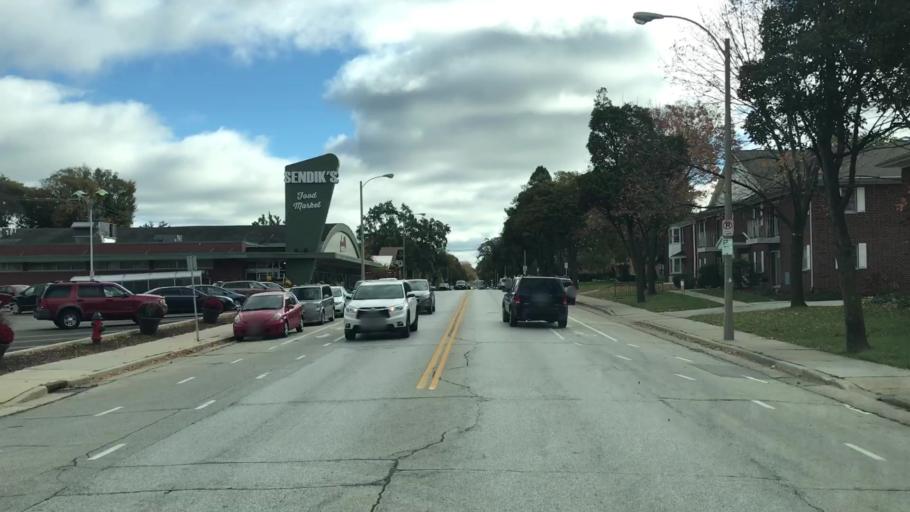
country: US
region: Wisconsin
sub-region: Milwaukee County
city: Wauwatosa
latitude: 43.0604
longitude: -88.0210
